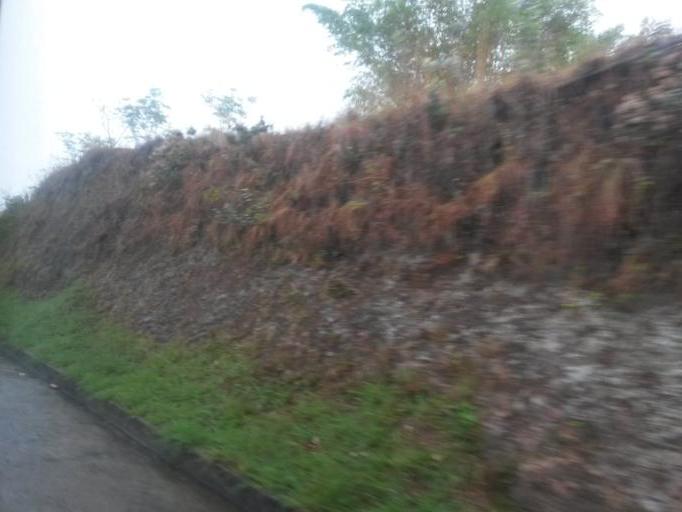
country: CO
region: Cauca
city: El Bordo
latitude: 2.1535
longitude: -76.9143
